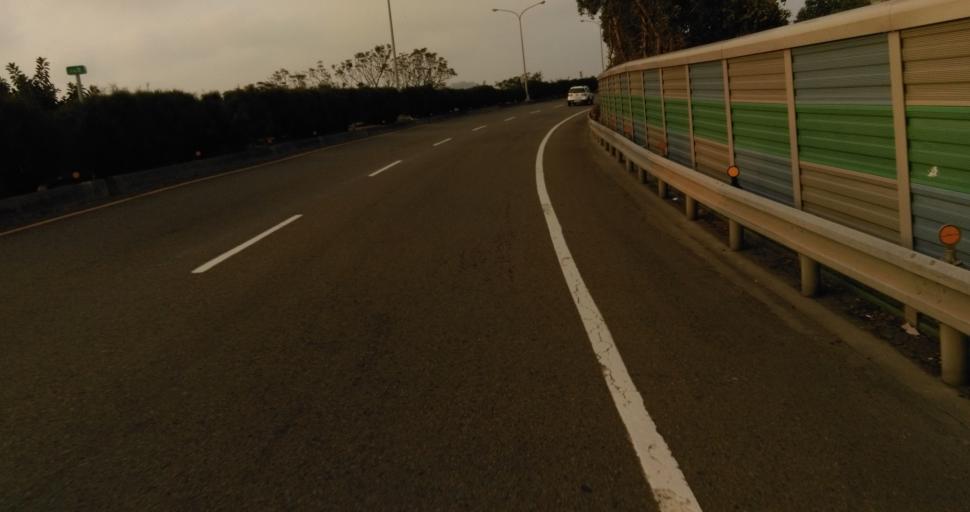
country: TW
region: Taiwan
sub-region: Hsinchu
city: Hsinchu
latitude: 24.8073
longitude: 120.9182
